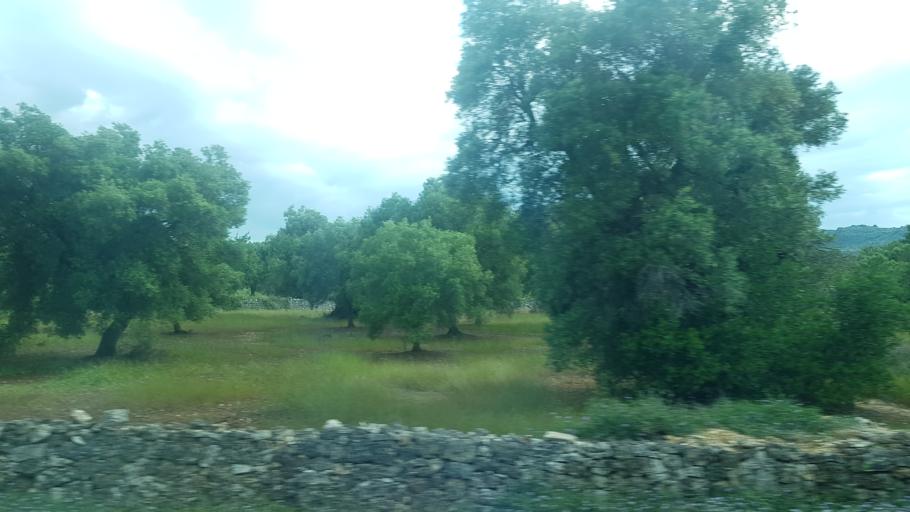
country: IT
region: Apulia
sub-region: Provincia di Brindisi
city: Ostuni
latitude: 40.7541
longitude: 17.5748
